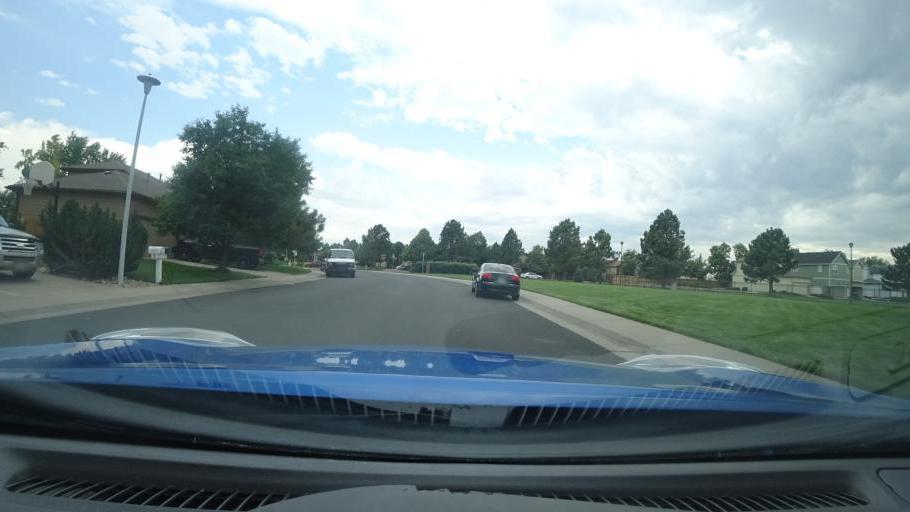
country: US
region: Colorado
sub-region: Adams County
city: Aurora
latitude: 39.6864
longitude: -104.7879
